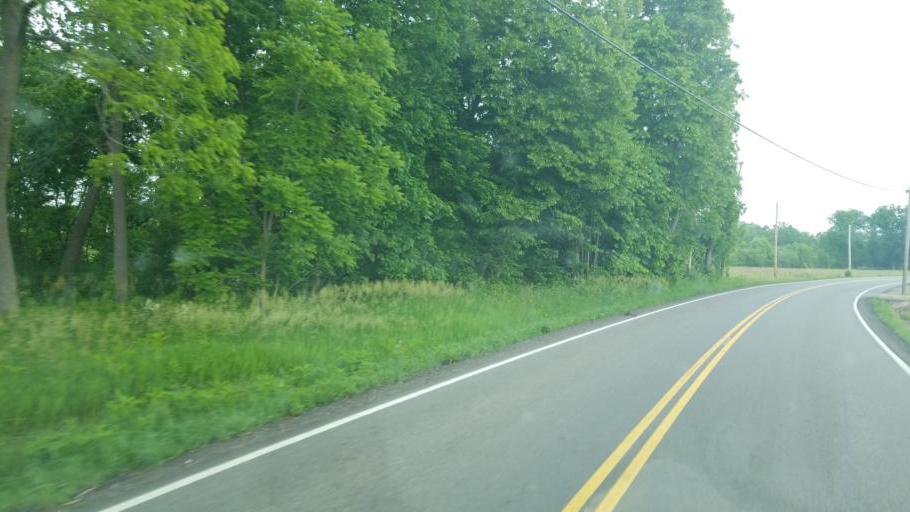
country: US
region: Ohio
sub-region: Knox County
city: Danville
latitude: 40.4956
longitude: -82.2866
